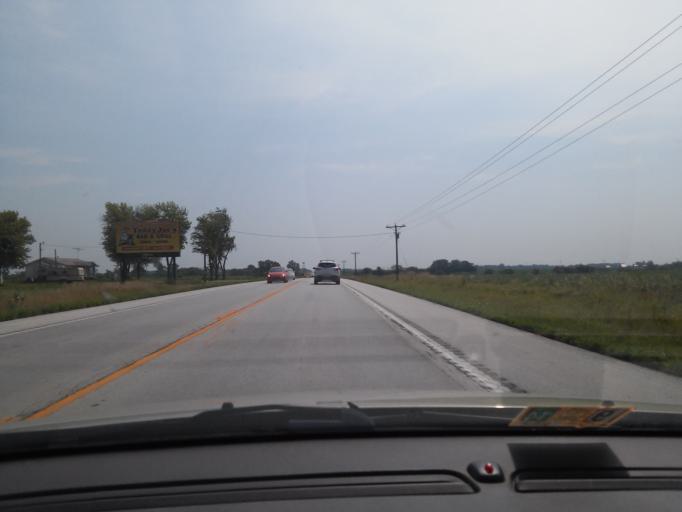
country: US
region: Missouri
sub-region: Montgomery County
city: Wellsville
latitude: 39.1633
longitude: -91.6686
